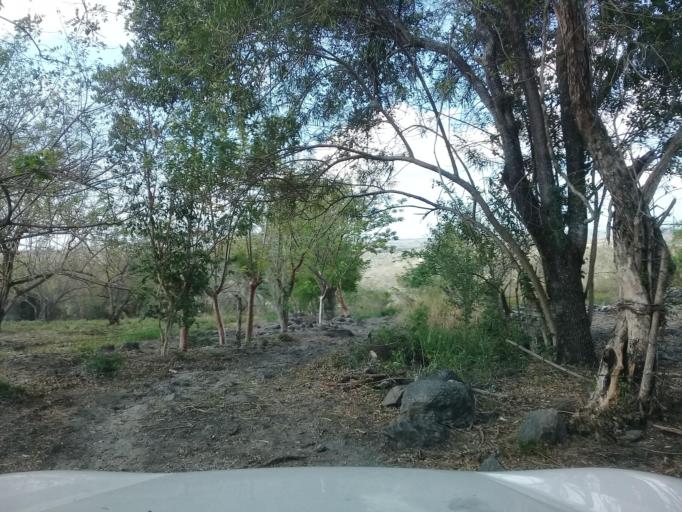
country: MX
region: Veracruz
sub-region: Emiliano Zapata
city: Plan del Rio
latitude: 19.4093
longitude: -96.6513
